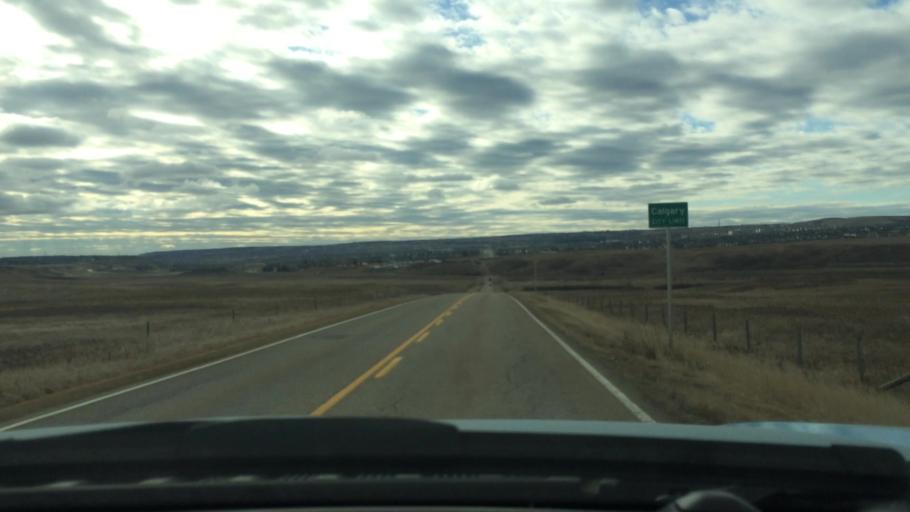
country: CA
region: Alberta
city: Airdrie
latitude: 51.1970
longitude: -114.1412
